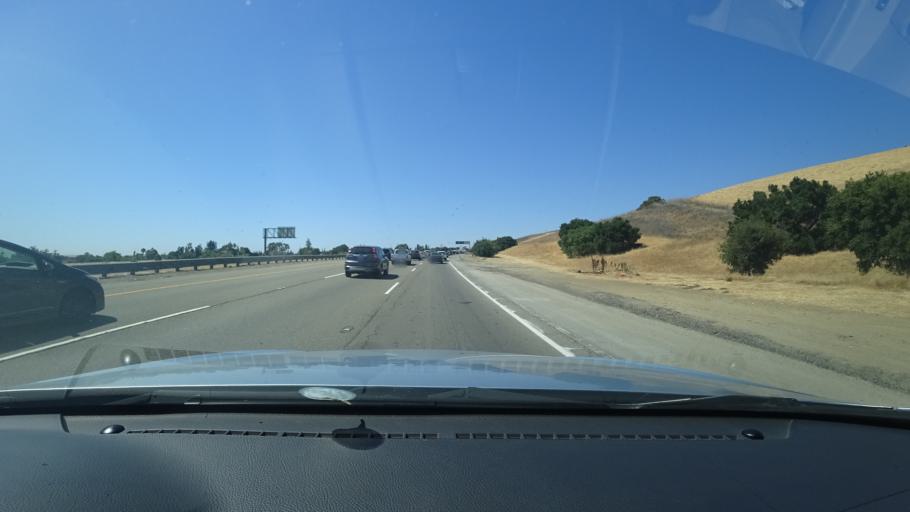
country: US
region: California
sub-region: Santa Clara County
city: Milpitas
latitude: 37.4721
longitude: -121.9097
